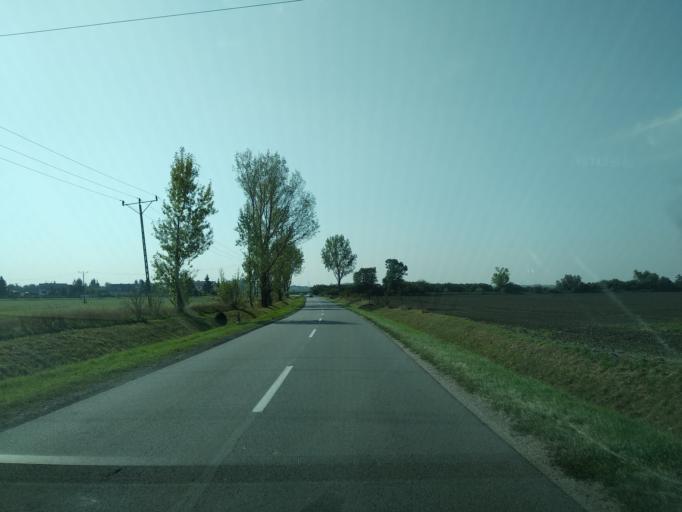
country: PL
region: Lower Silesian Voivodeship
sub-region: Powiat wroclawski
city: Zerniki Wroclawskie
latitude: 51.0387
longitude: 17.0299
